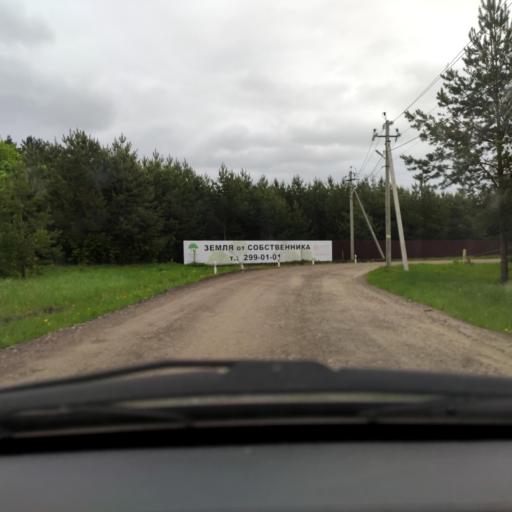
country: RU
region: Bashkortostan
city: Kabakovo
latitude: 54.6223
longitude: 56.1641
